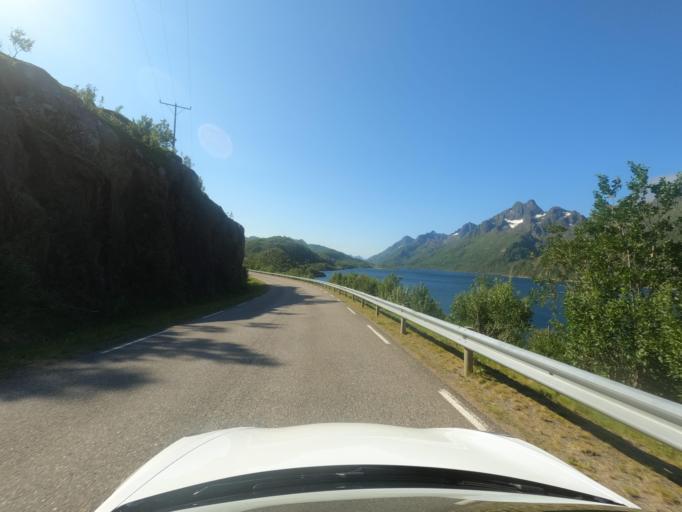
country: NO
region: Nordland
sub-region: Hadsel
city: Stokmarknes
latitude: 68.4490
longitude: 15.2032
